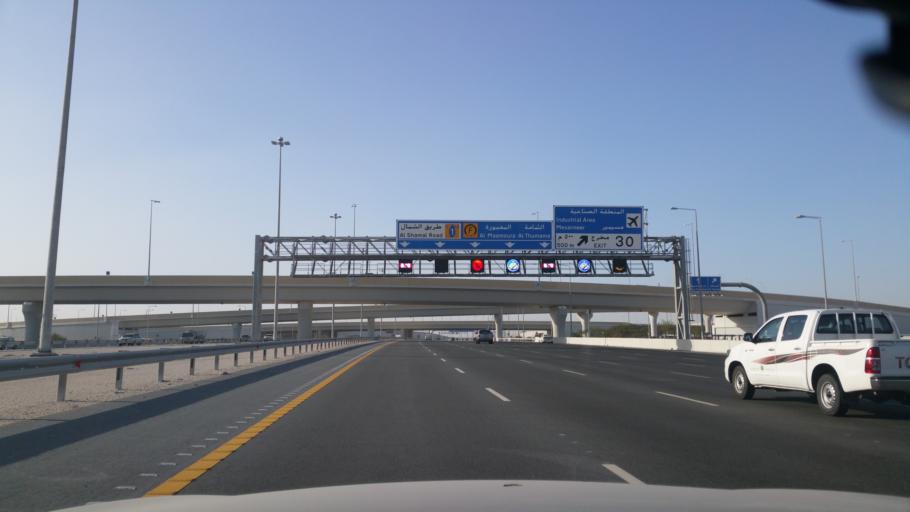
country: QA
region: Al Wakrah
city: Al Wukayr
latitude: 25.1805
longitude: 51.5503
